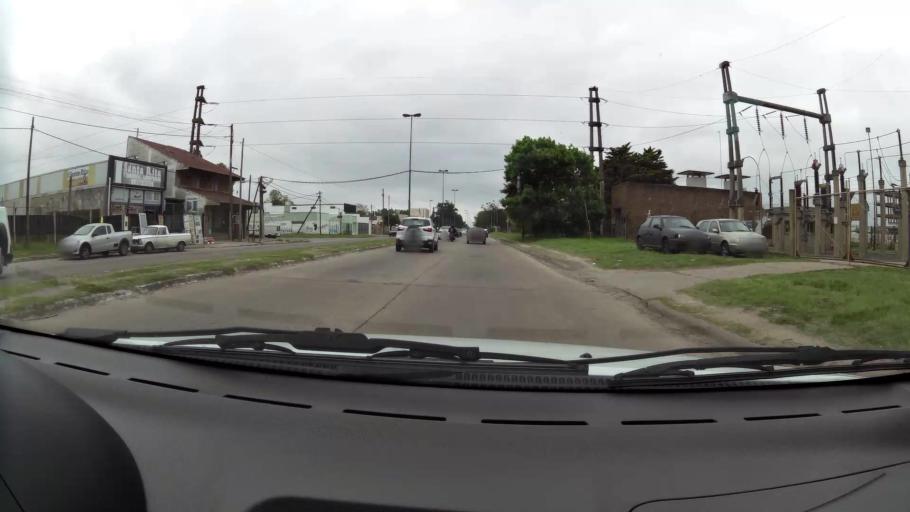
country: AR
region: Buenos Aires
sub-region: Partido de La Plata
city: La Plata
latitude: -34.9825
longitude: -58.0341
